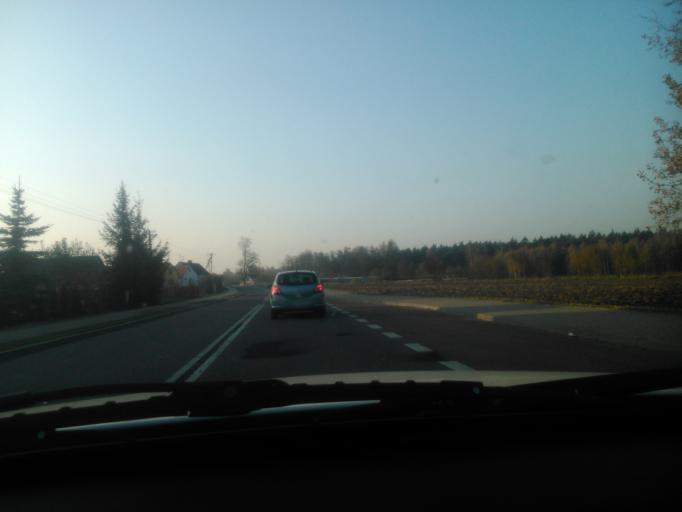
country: PL
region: Masovian Voivodeship
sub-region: Powiat mlawski
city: Szydlowo
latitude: 53.0777
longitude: 20.5202
